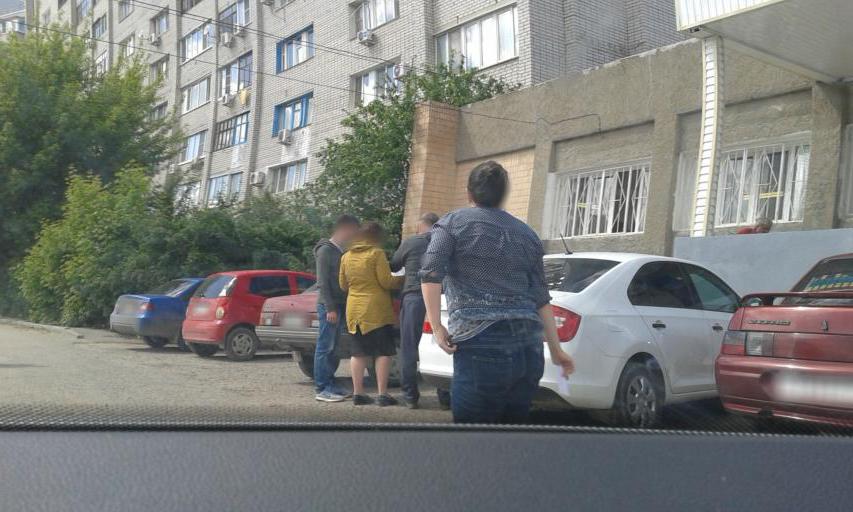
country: RU
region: Volgograd
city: Volgograd
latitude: 48.6571
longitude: 44.4341
